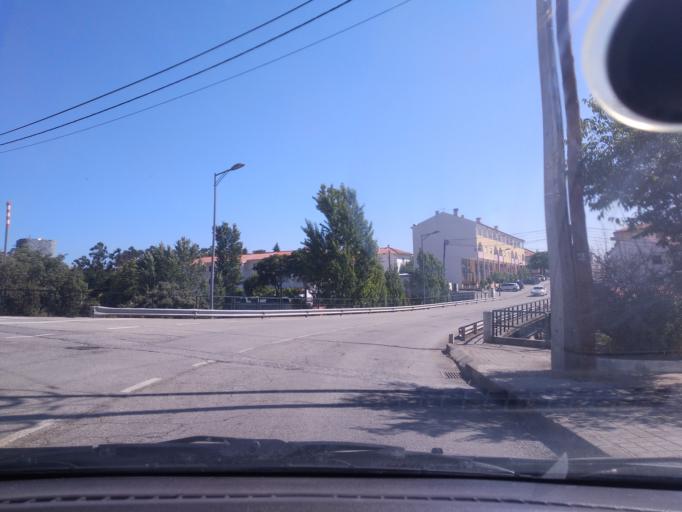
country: PT
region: Portalegre
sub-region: Nisa
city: Nisa
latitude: 39.6539
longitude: -7.6695
